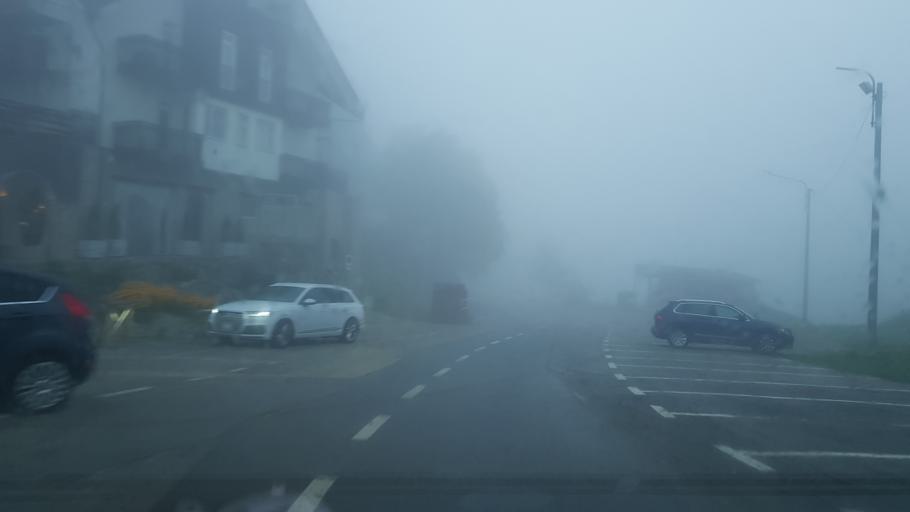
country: IT
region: Piedmont
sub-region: Provincia di Cuneo
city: Frabosa Soprana
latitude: 44.2531
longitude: 7.7801
